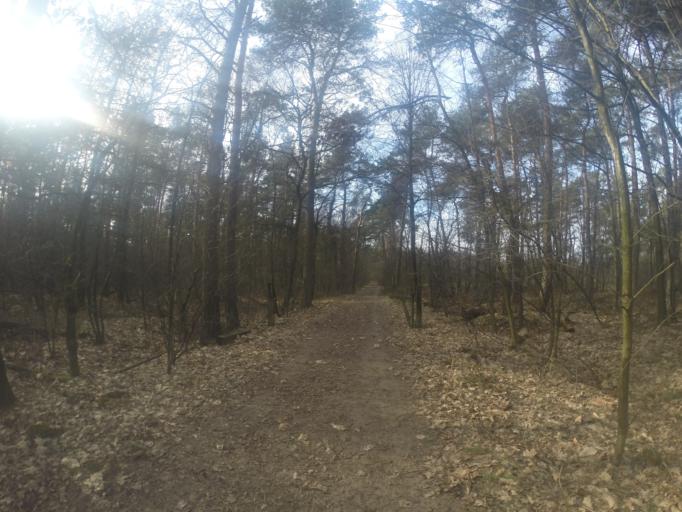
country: NL
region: Gelderland
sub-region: Gemeente Lochem
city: Lochem
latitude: 52.1339
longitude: 6.3615
